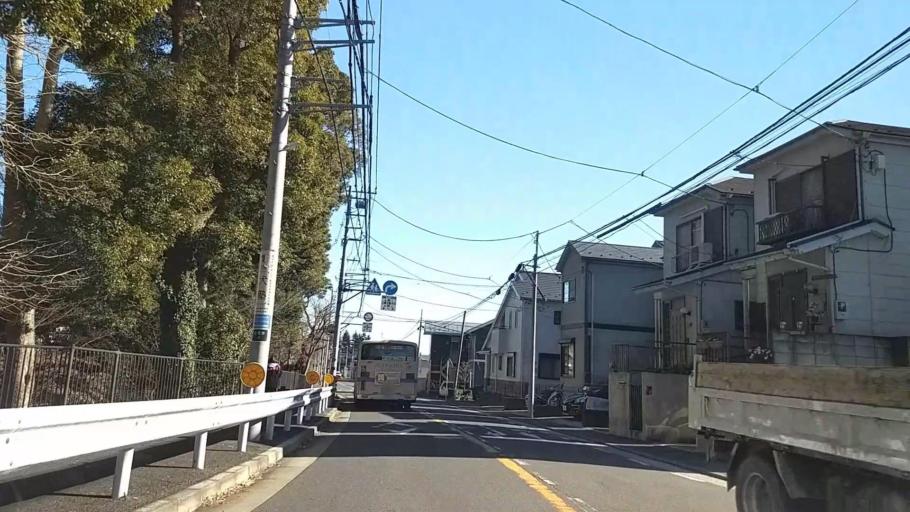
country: JP
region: Kanagawa
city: Yokohama
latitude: 35.4517
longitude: 139.5820
